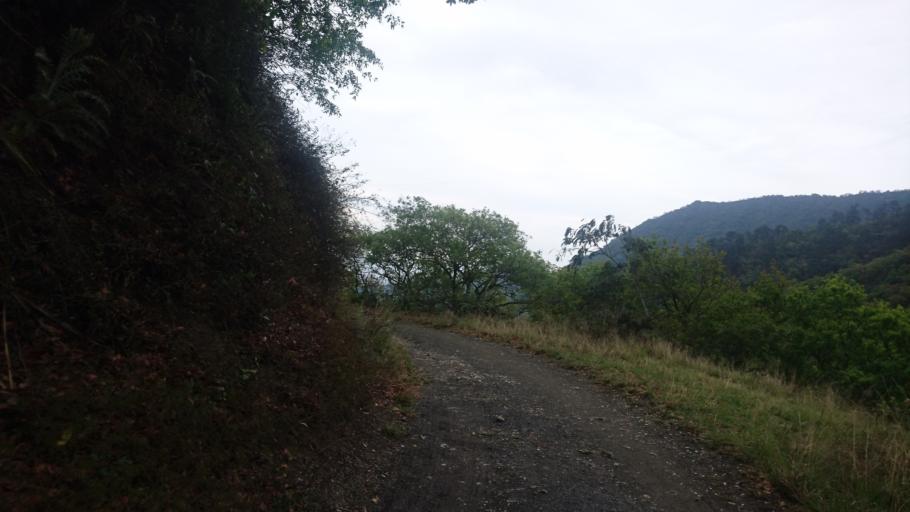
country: MX
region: Nuevo Leon
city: Garza Garcia
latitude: 25.6043
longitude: -100.3402
